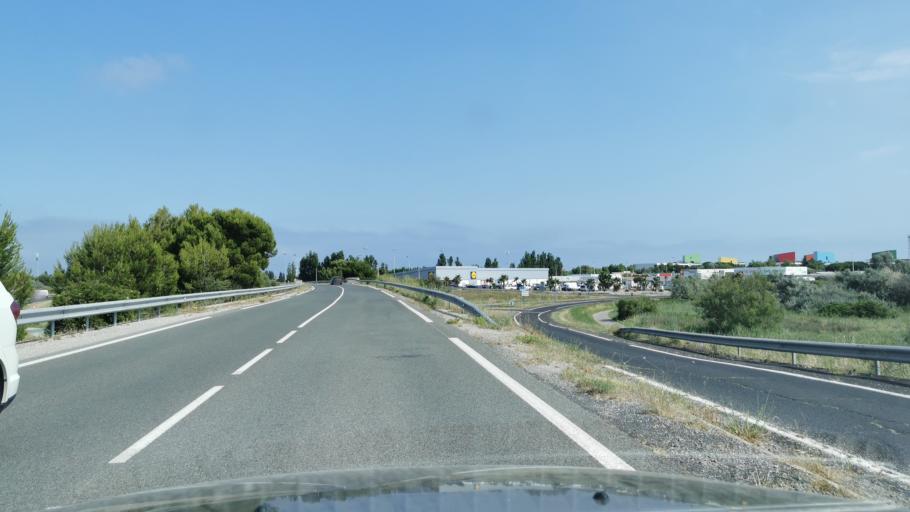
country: FR
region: Languedoc-Roussillon
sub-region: Departement de l'Aude
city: Gruissan
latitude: 43.1193
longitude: 3.1034
